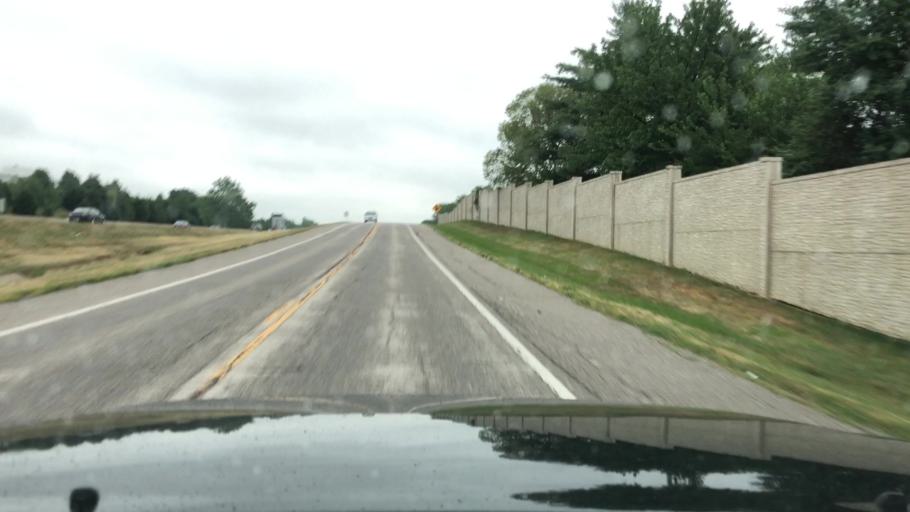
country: US
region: Missouri
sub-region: Saint Charles County
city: Lake Saint Louis
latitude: 38.8044
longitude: -90.7901
